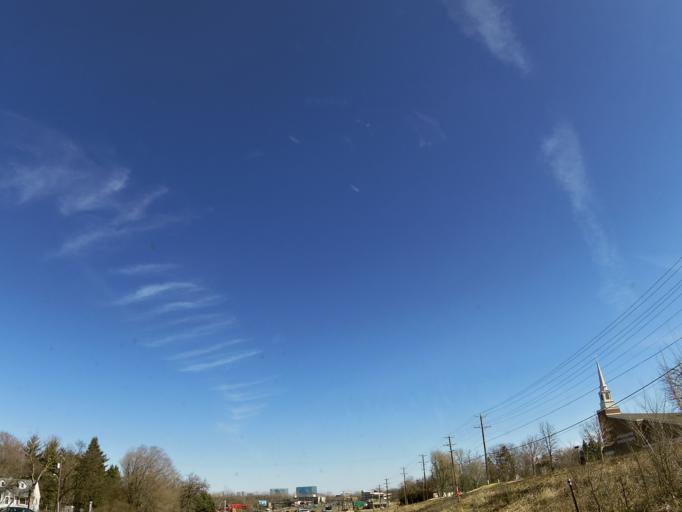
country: US
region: Minnesota
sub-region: Hennepin County
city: Plymouth
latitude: 44.9897
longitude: -93.4283
